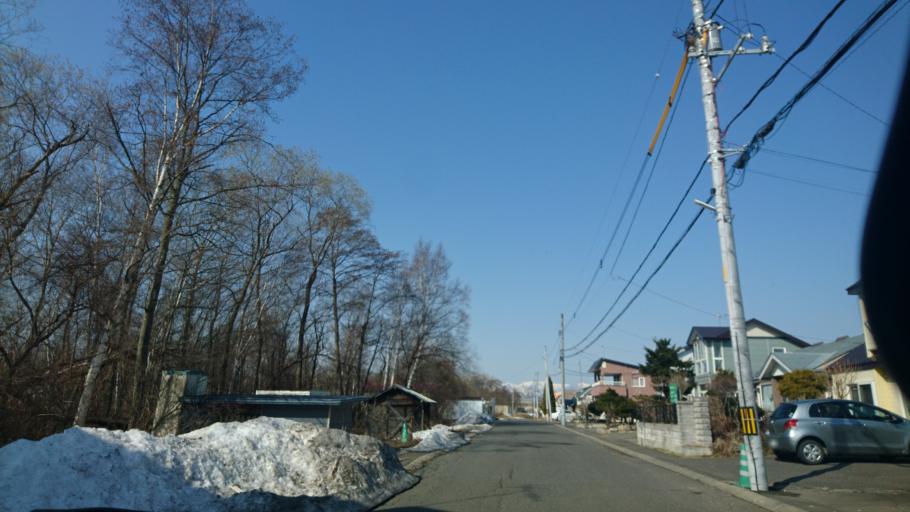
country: JP
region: Hokkaido
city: Obihiro
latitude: 42.9132
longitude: 143.1155
